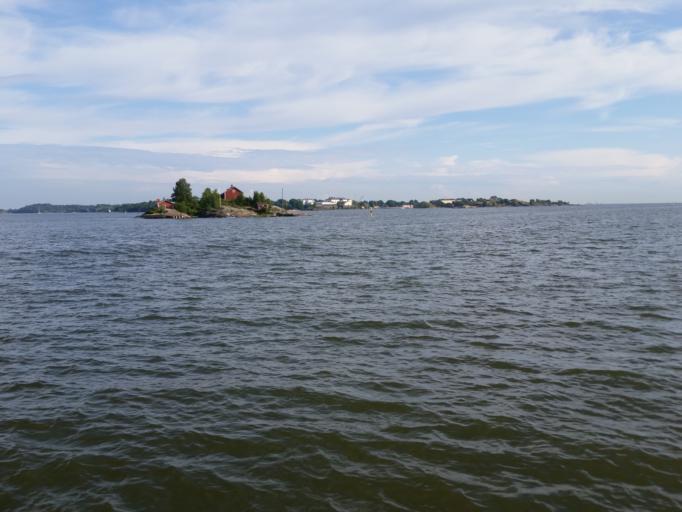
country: FI
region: Uusimaa
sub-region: Helsinki
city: Helsinki
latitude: 60.1619
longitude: 24.9691
